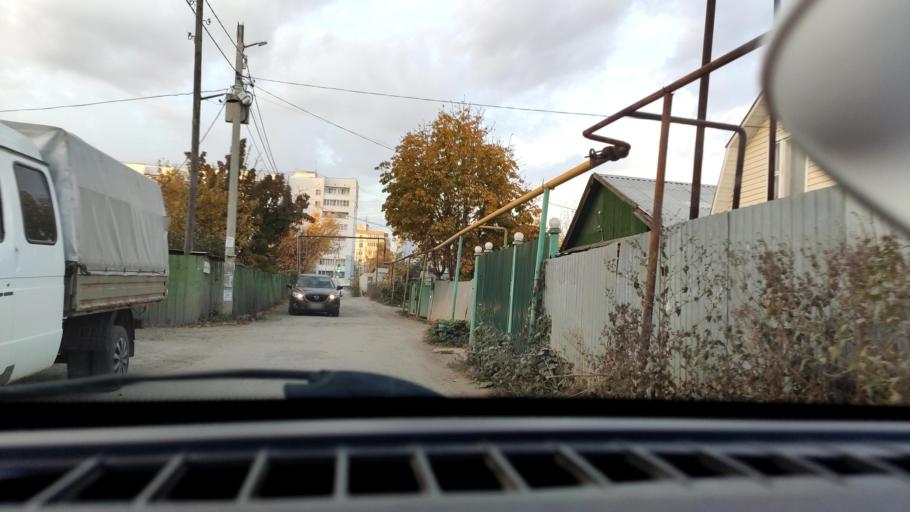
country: RU
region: Samara
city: Samara
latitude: 53.2684
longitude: 50.2283
